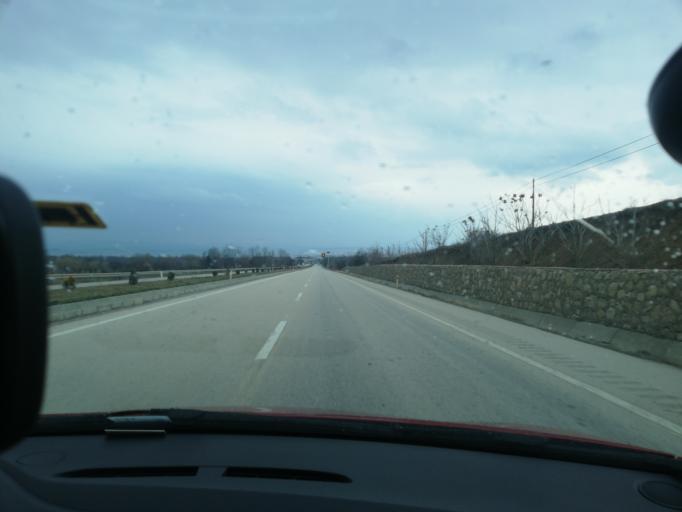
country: TR
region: Kastamonu
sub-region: Cide
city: Kastamonu
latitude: 41.4912
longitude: 33.7606
